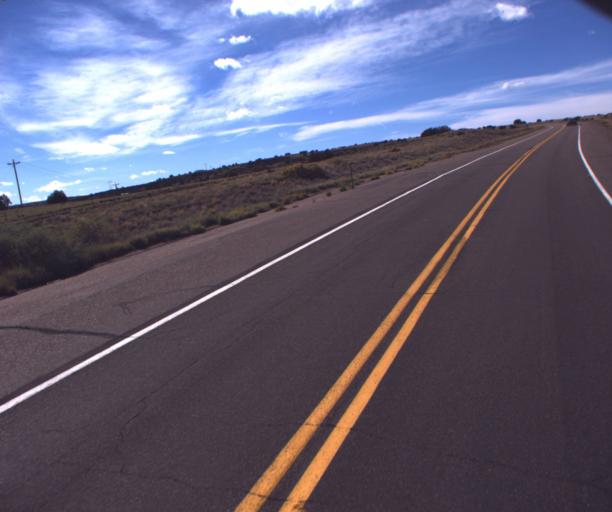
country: US
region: Arizona
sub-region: Apache County
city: Saint Johns
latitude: 34.4994
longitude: -109.4951
